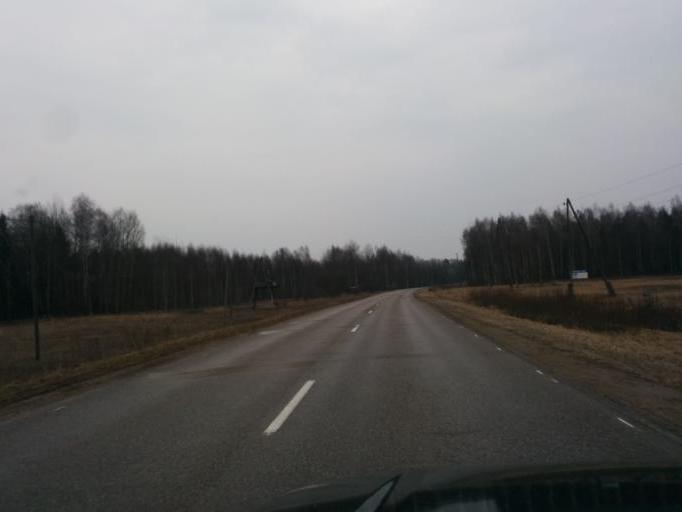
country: LV
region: Ikskile
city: Ikskile
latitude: 56.8177
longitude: 24.4640
